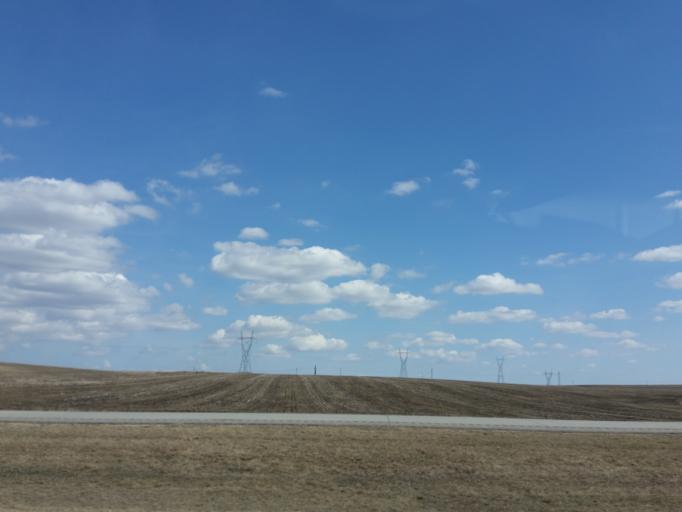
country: US
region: South Dakota
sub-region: Codington County
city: Watertown
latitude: 44.9762
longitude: -97.0552
